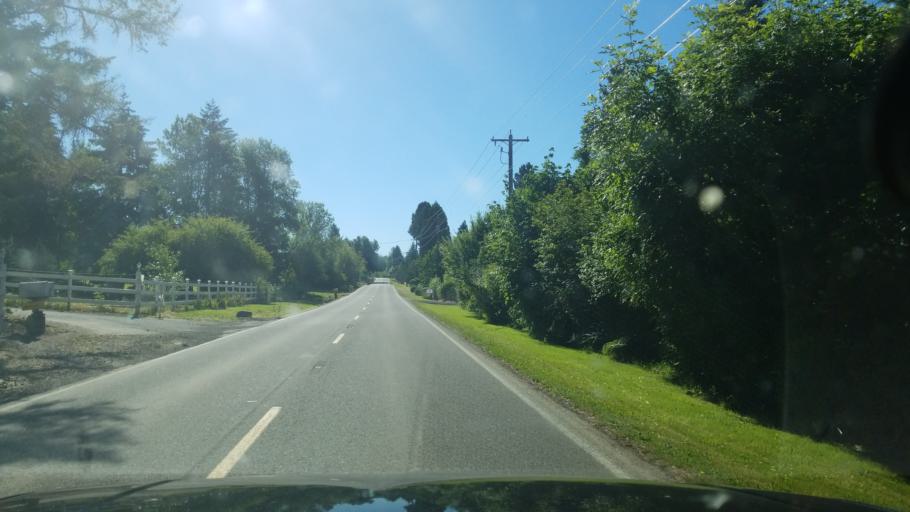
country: US
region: Oregon
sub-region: Yamhill County
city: McMinnville
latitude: 45.2260
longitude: -123.2659
